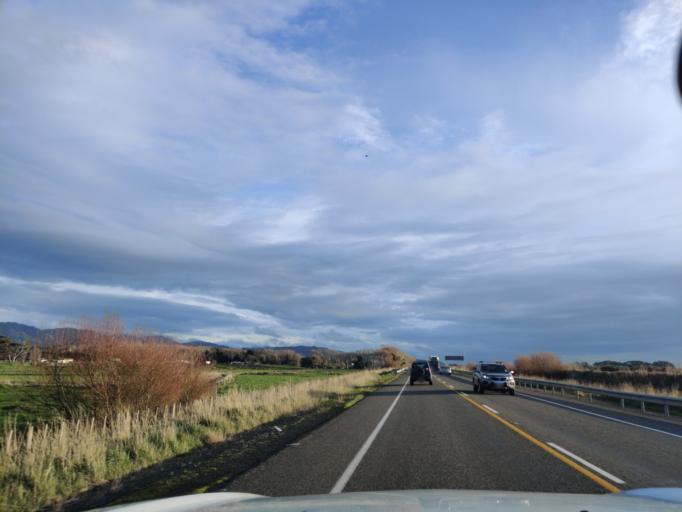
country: NZ
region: Manawatu-Wanganui
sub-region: Horowhenua District
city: Foxton
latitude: -40.5158
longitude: 175.4512
